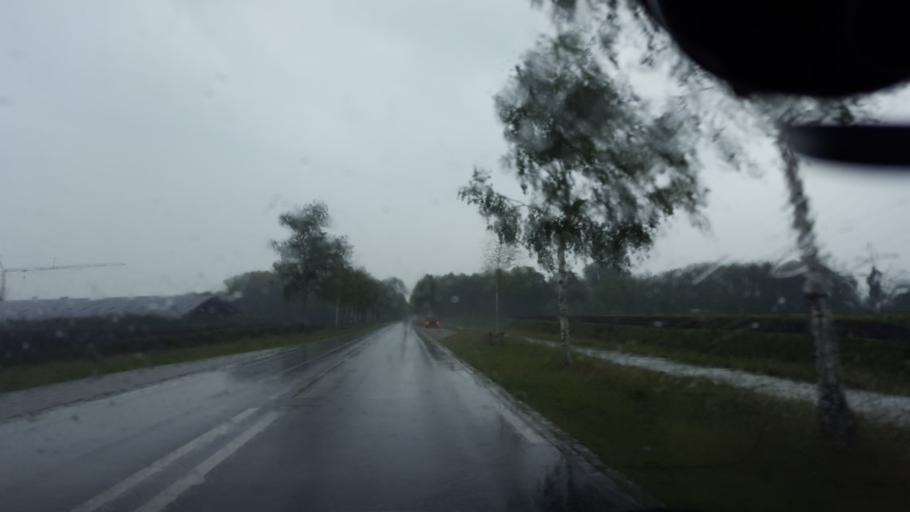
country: NL
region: North Brabant
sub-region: Gemeente Someren
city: Someren
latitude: 51.3902
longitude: 5.6826
